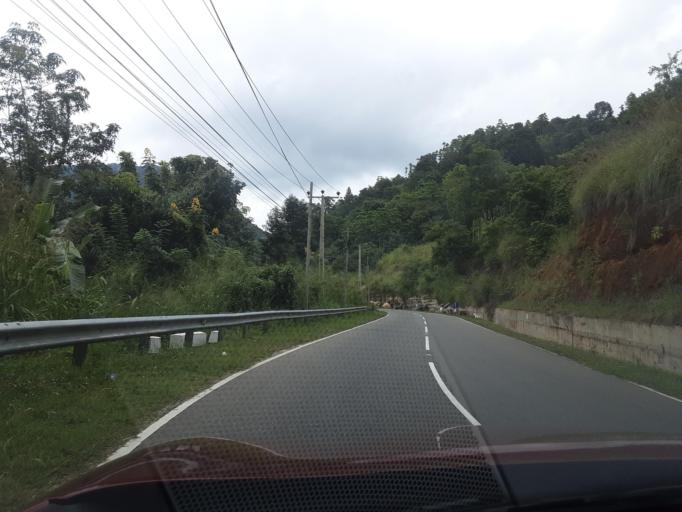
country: LK
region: Uva
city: Badulla
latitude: 6.9312
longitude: 81.1962
